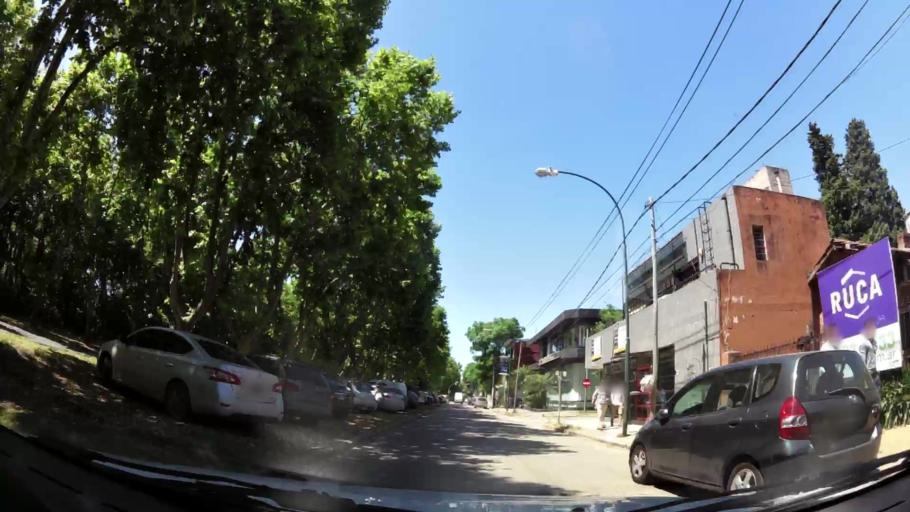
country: AR
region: Buenos Aires
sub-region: Partido de San Isidro
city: San Isidro
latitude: -34.4923
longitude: -58.5295
